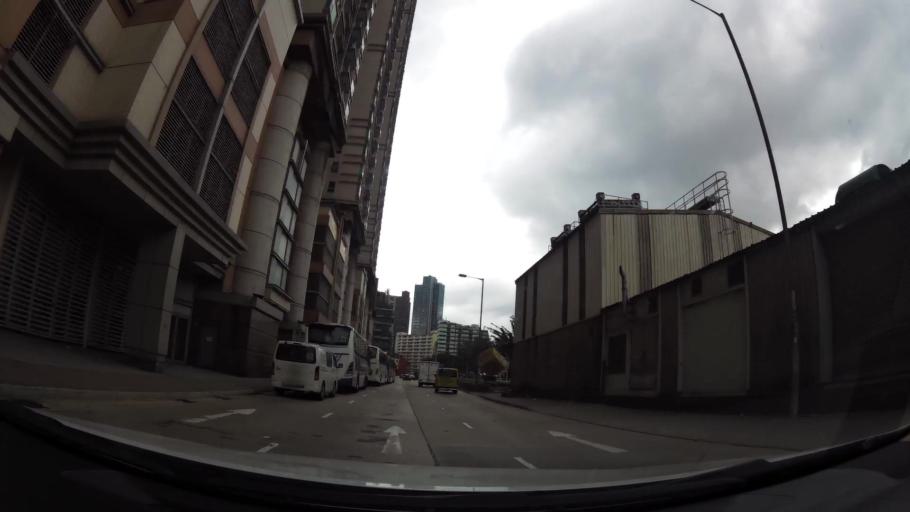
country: HK
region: Kowloon City
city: Kowloon
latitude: 22.3235
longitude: 114.1912
